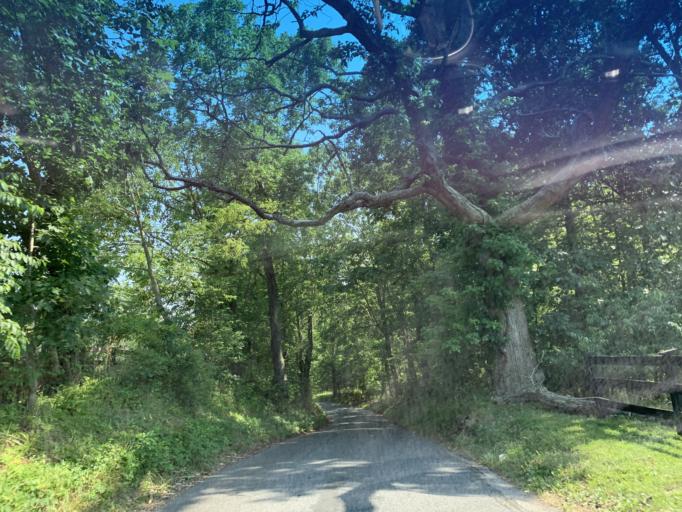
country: US
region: Maryland
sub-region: Montgomery County
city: Poolesville
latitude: 39.1512
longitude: -77.4540
